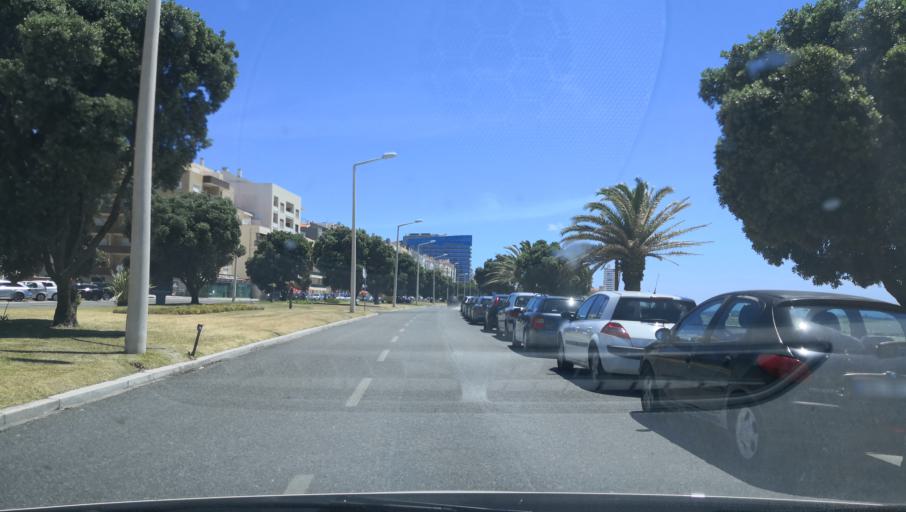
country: PT
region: Coimbra
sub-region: Figueira da Foz
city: Buarcos
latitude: 40.1606
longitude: -8.8711
